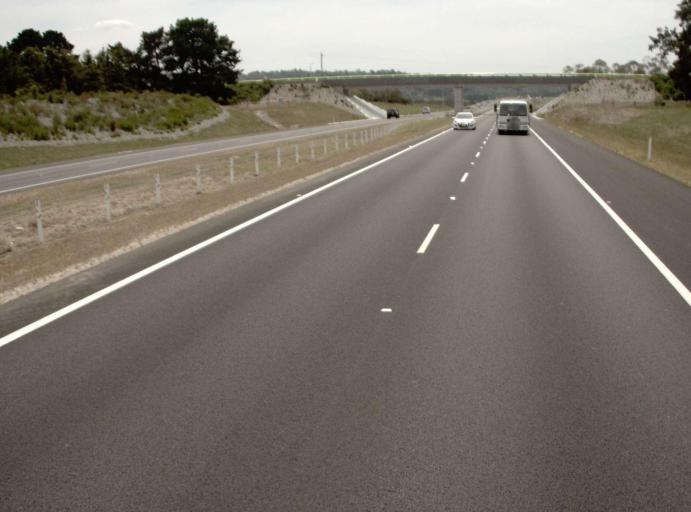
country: AU
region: Victoria
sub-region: Mornington Peninsula
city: Moorooduc
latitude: -38.2184
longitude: 145.1289
